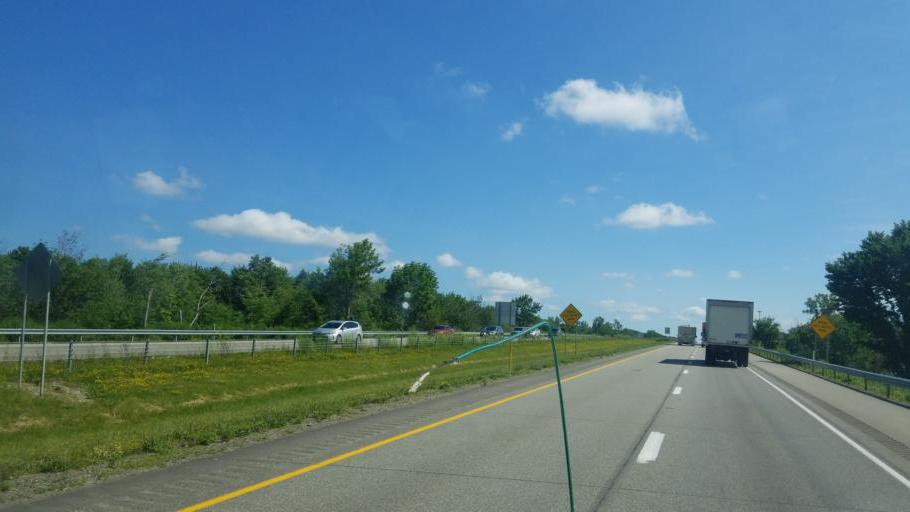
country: US
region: Pennsylvania
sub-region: Erie County
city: Wesleyville
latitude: 42.0760
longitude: -80.0302
